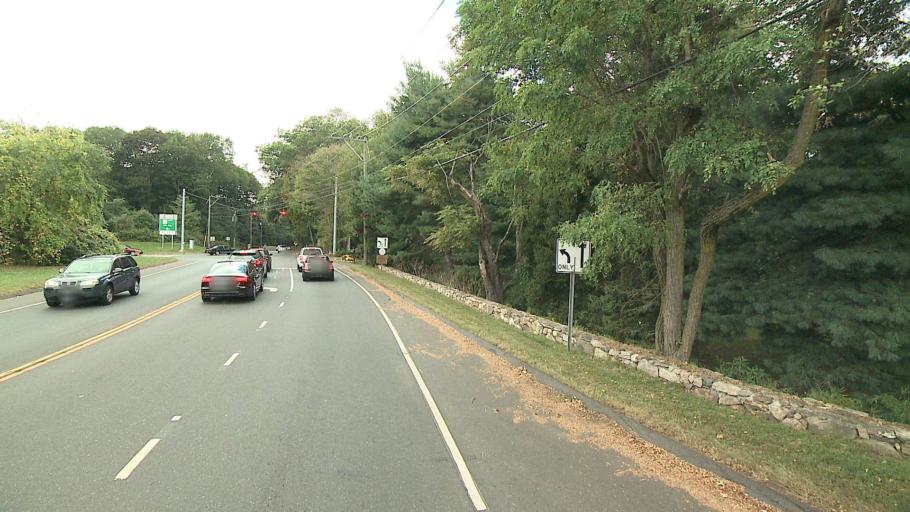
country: US
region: Connecticut
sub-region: Fairfield County
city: Westport
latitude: 41.1648
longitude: -73.3771
